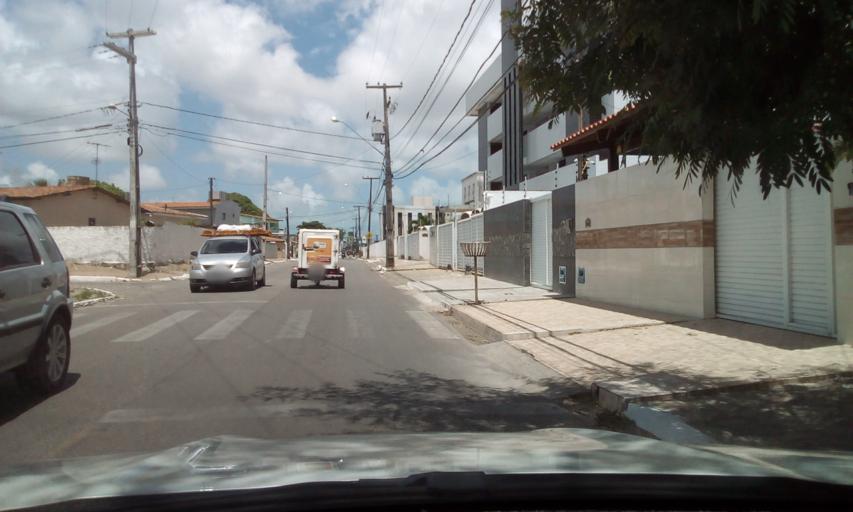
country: BR
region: Paraiba
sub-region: Joao Pessoa
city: Joao Pessoa
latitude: -7.1839
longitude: -34.8668
